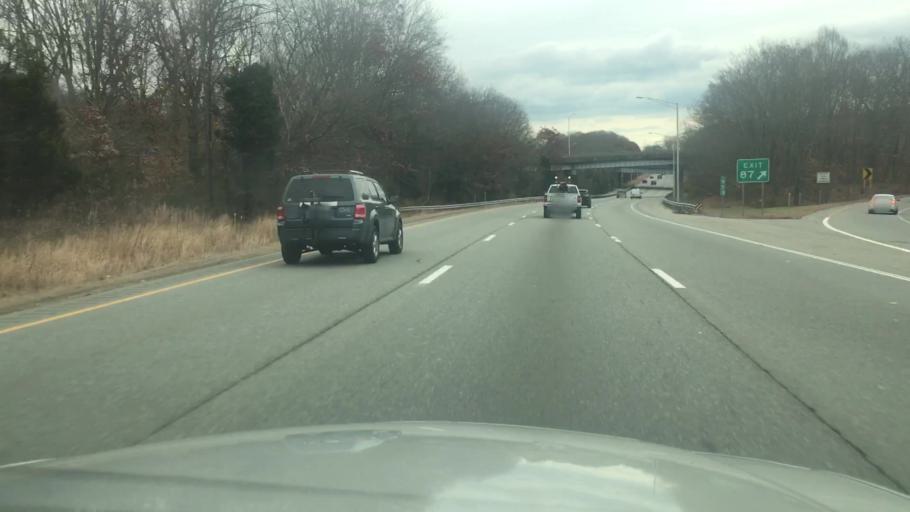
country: US
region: Connecticut
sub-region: New London County
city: Long Hill
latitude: 41.3621
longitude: -72.0598
